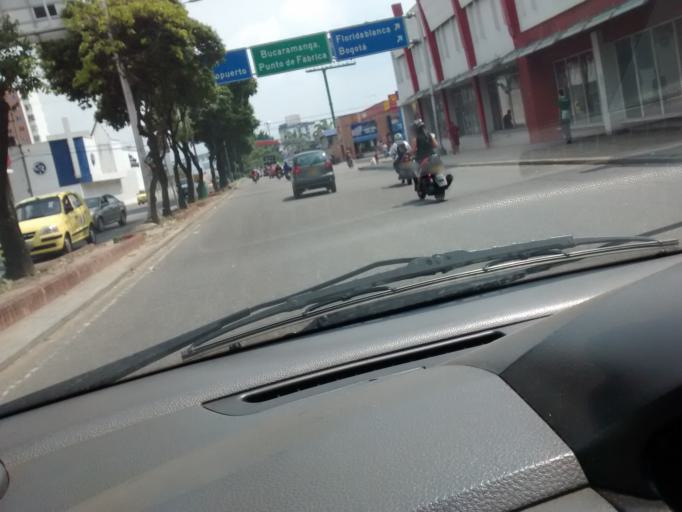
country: CO
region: Santander
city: Bucaramanga
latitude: 7.1089
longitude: -73.1143
